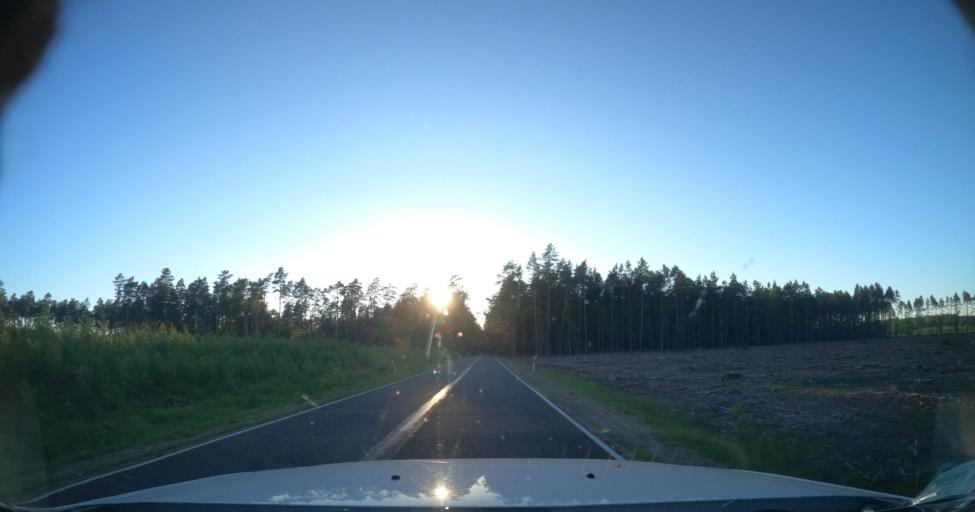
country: PL
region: Pomeranian Voivodeship
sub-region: Powiat slupski
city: Potegowo
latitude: 54.4027
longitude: 17.4555
